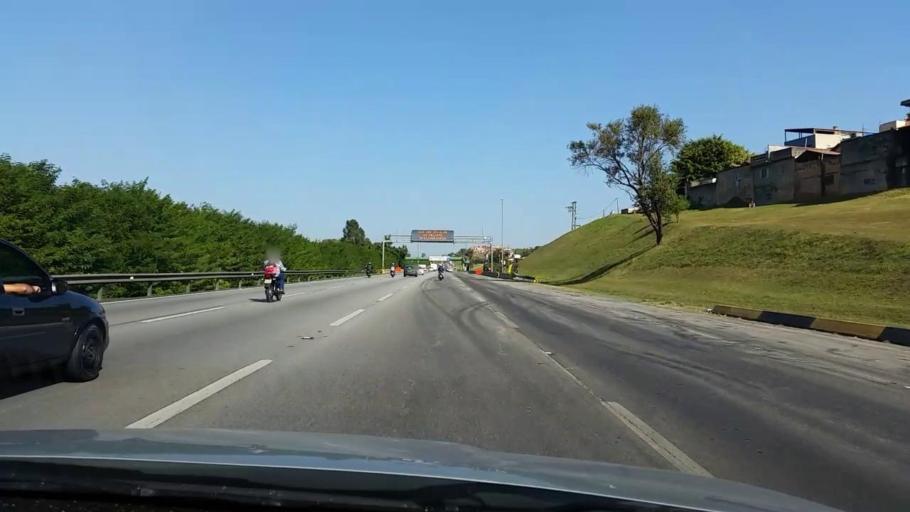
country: BR
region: Sao Paulo
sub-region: Diadema
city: Diadema
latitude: -23.6588
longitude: -46.6338
